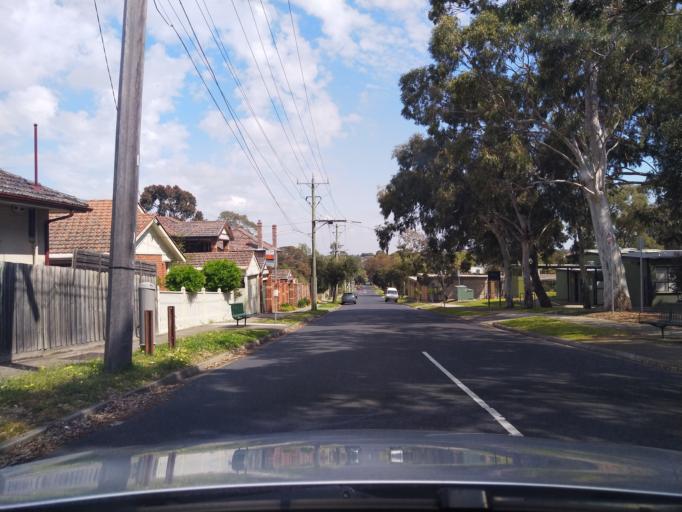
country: AU
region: Victoria
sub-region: Banyule
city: Bellfield
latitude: -37.7629
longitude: 145.0437
